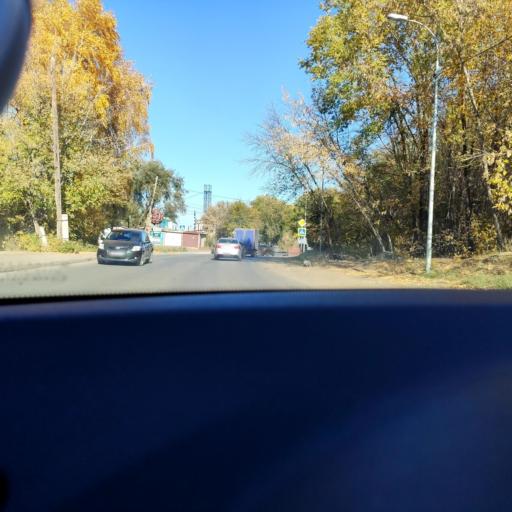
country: RU
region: Samara
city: Petra-Dubrava
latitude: 53.2358
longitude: 50.2942
